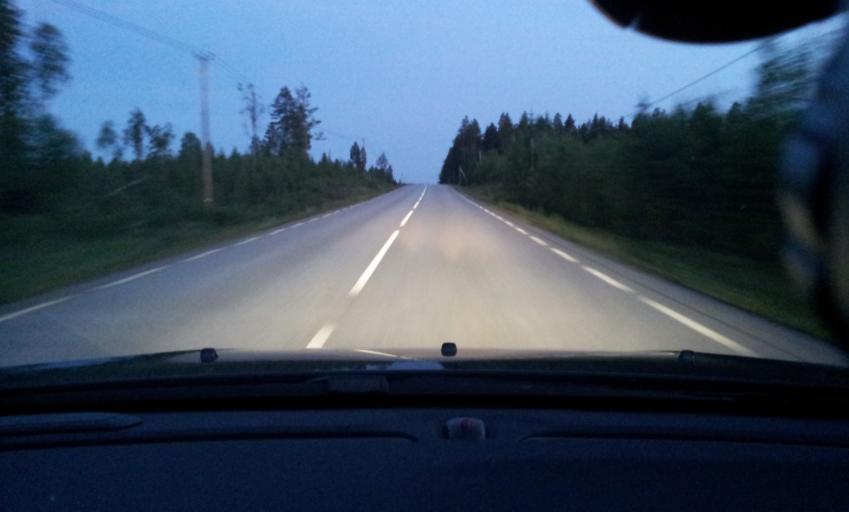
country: SE
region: Jaemtland
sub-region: OEstersunds Kommun
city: Brunflo
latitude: 62.7341
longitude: 14.9802
